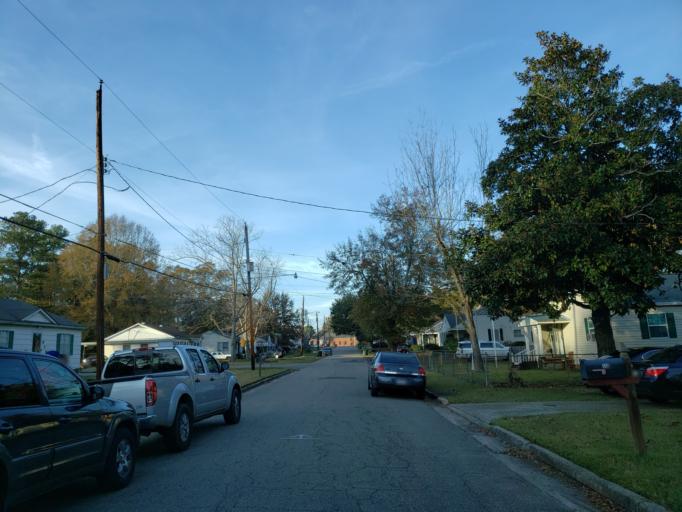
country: US
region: Mississippi
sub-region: Forrest County
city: Hattiesburg
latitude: 31.3298
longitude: -89.3191
